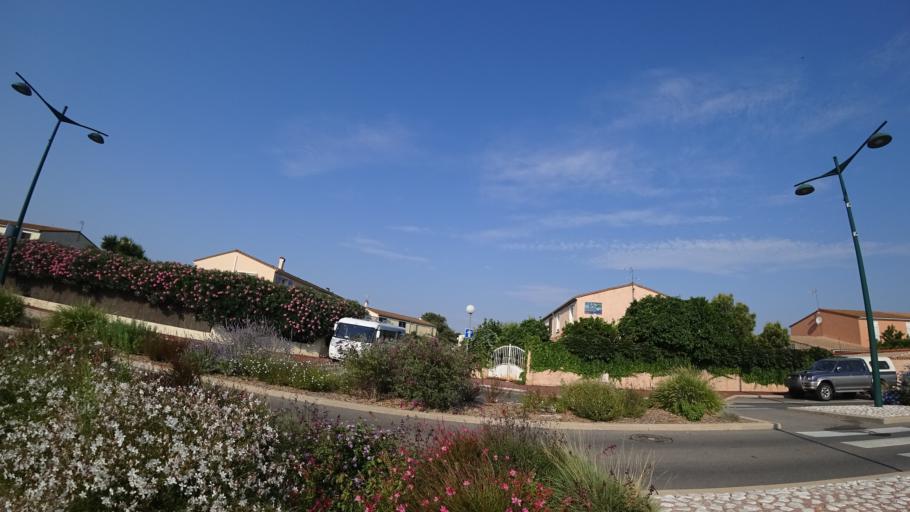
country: FR
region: Languedoc-Roussillon
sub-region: Departement des Pyrenees-Orientales
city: Bompas
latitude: 42.7267
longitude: 2.9359
